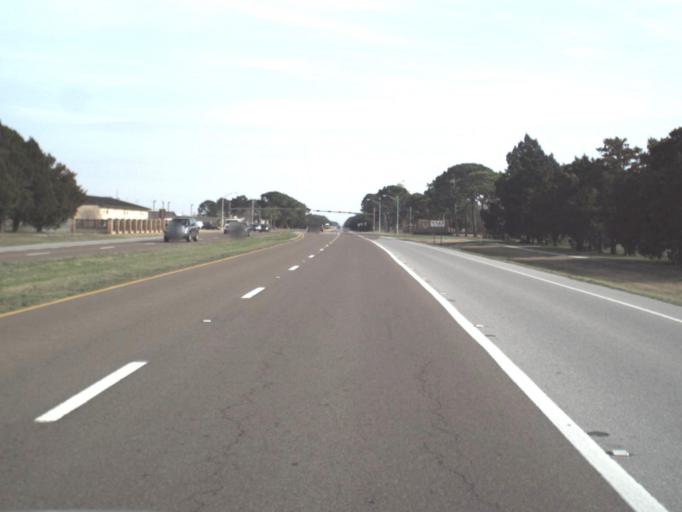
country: US
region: Florida
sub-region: Bay County
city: Tyndall Air Force Base
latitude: 30.0719
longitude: -85.5929
